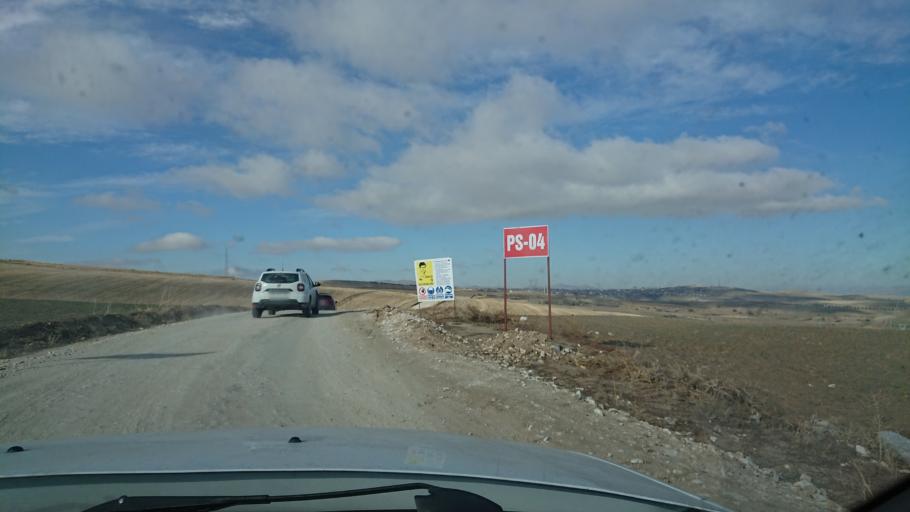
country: TR
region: Aksaray
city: Agacoren
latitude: 38.8483
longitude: 33.9499
